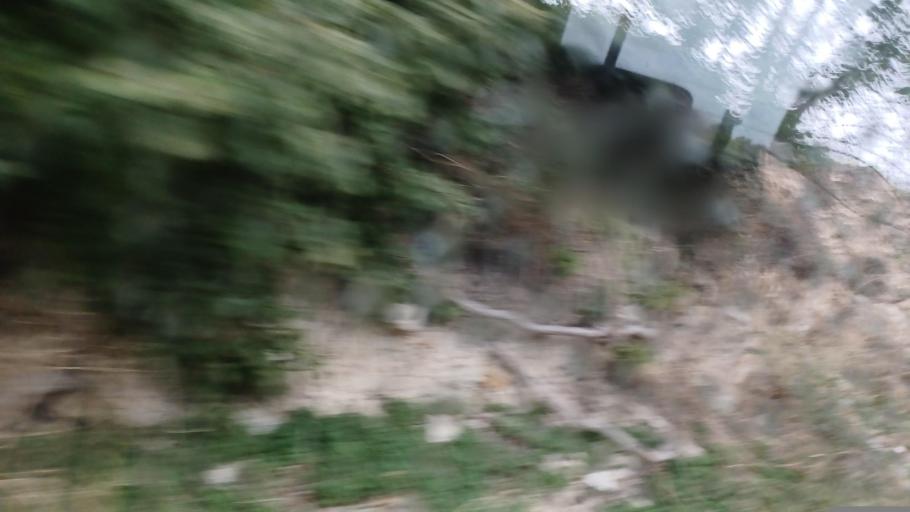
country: CY
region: Pafos
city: Mesogi
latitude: 34.8727
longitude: 32.5514
